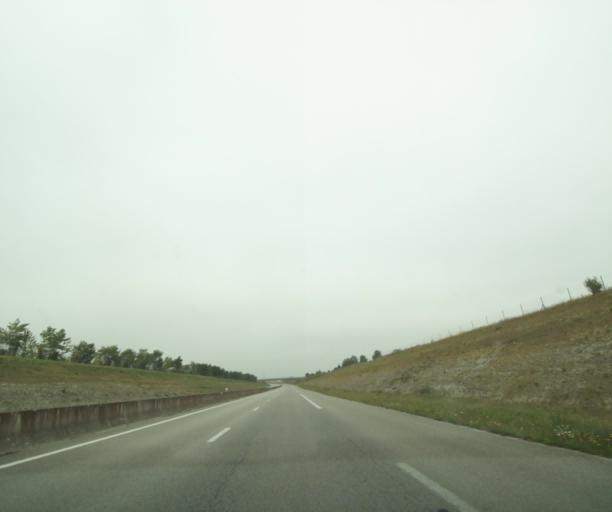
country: FR
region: Lower Normandy
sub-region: Departement de l'Orne
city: Mortree
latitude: 48.6504
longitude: 0.1213
